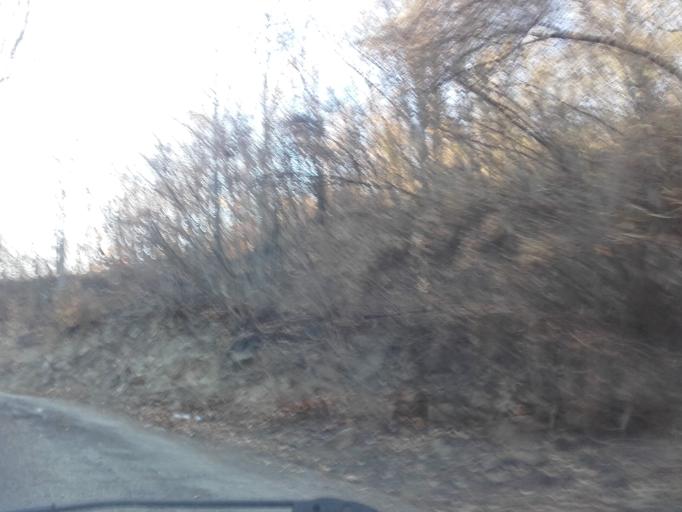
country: IT
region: Piedmont
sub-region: Provincia di Torino
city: Bussoleno
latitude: 45.1536
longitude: 7.1381
